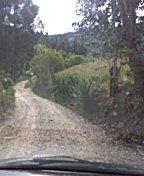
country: CO
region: Boyaca
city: Duitama
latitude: 5.8265
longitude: -73.0844
